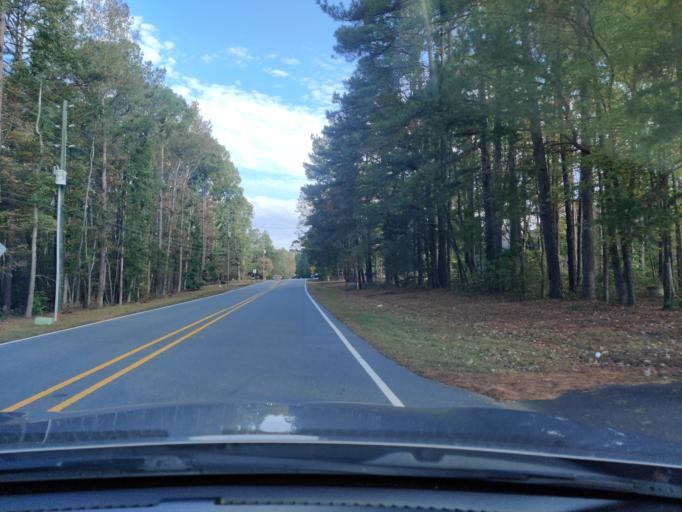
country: US
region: North Carolina
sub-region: Wake County
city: West Raleigh
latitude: 35.9082
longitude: -78.7038
